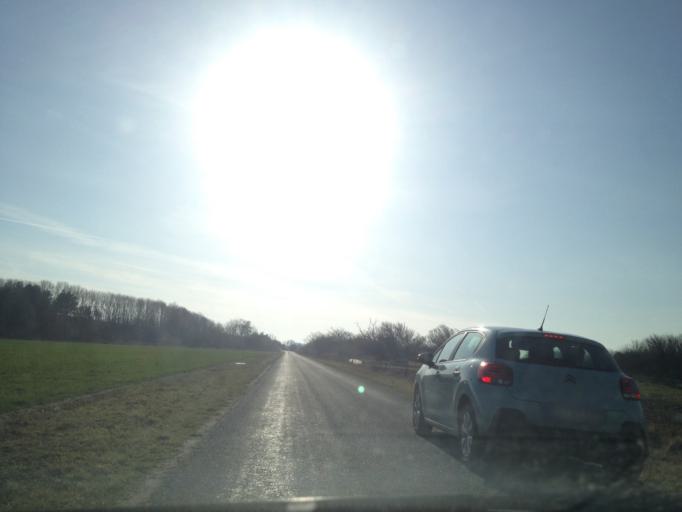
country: DK
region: South Denmark
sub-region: Kerteminde Kommune
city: Kerteminde
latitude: 55.5481
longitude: 10.6284
